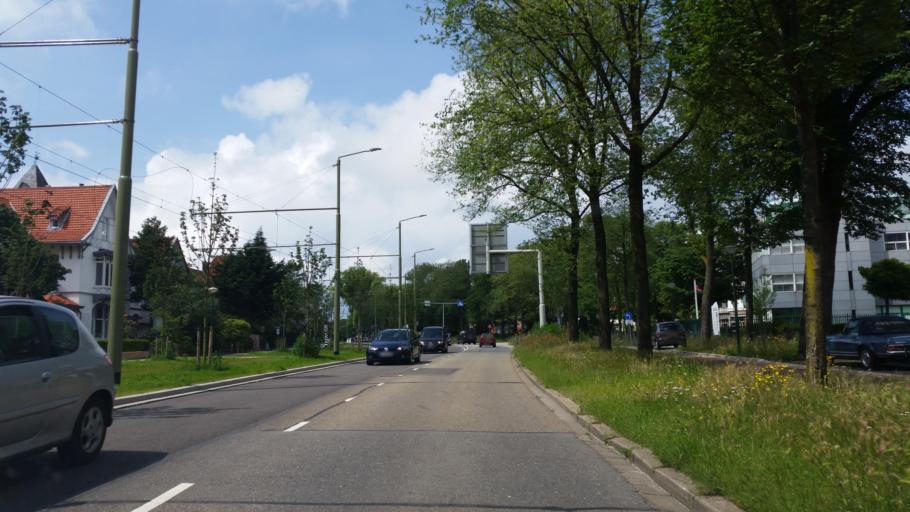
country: NL
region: South Holland
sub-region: Gemeente Den Haag
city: Scheveningen
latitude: 52.1008
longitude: 4.2984
